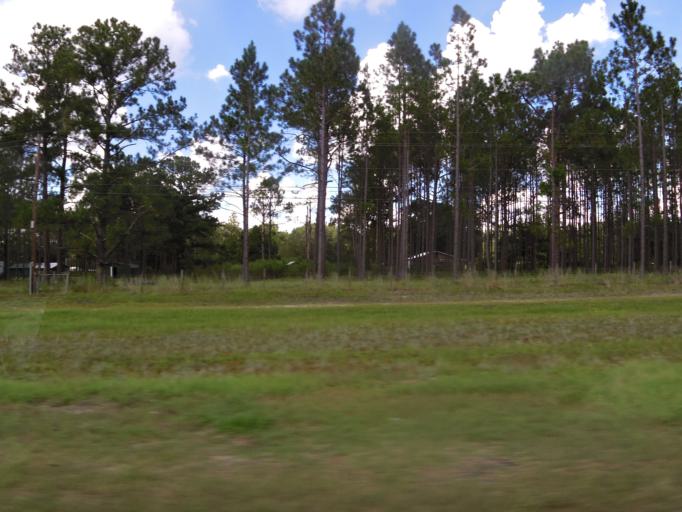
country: US
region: Georgia
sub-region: Echols County
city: Statenville
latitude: 30.7019
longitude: -83.0087
